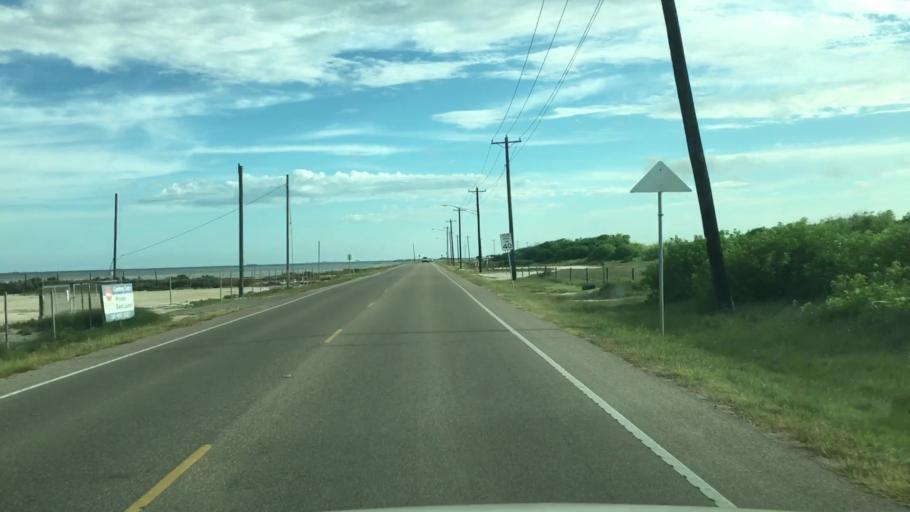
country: US
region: Texas
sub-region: Nueces County
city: Corpus Christi
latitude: 27.6565
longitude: -97.2776
